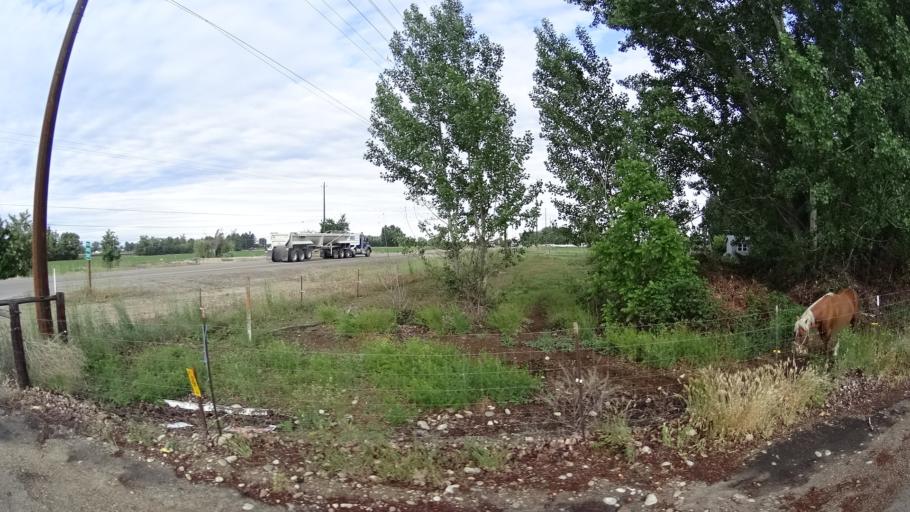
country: US
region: Idaho
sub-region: Ada County
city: Star
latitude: 43.6942
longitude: -116.5128
